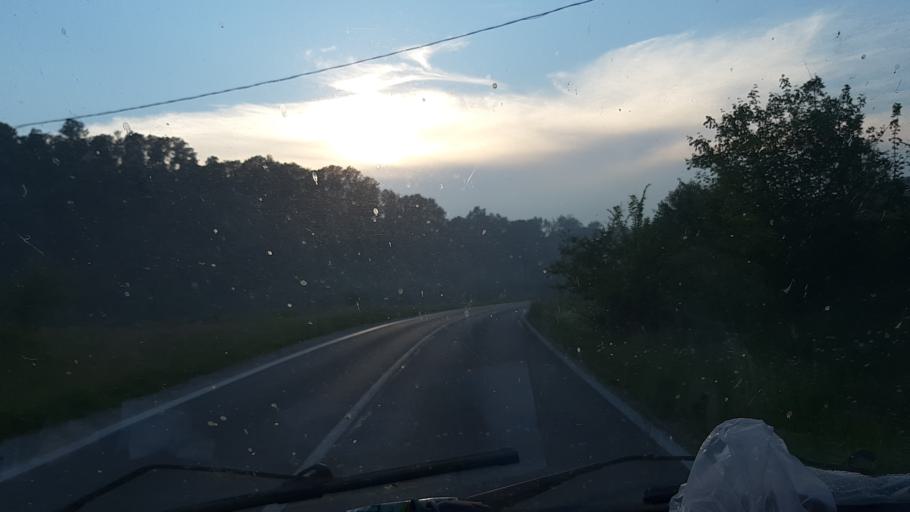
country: RO
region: Caras-Severin
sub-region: Municipiul Resita
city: Calnic
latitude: 45.3694
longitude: 21.8000
